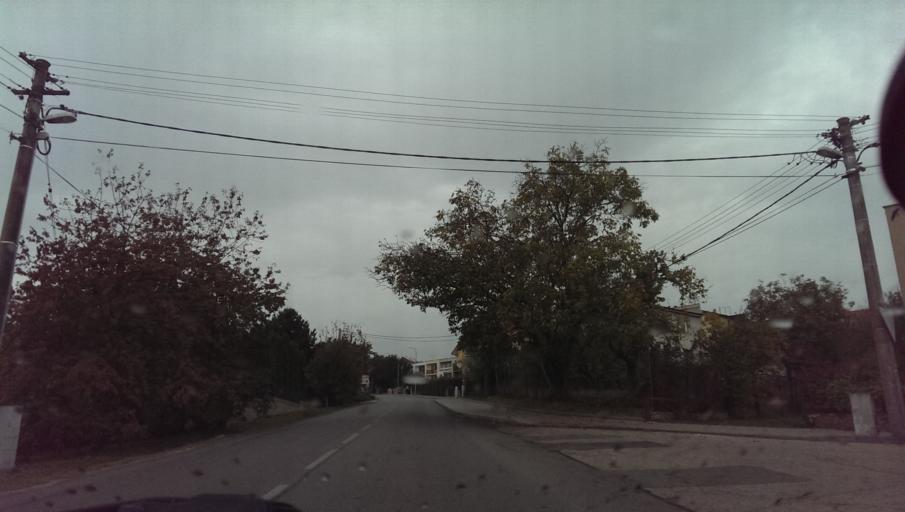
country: CZ
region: South Moravian
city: Moravany
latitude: 49.1473
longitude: 16.5744
